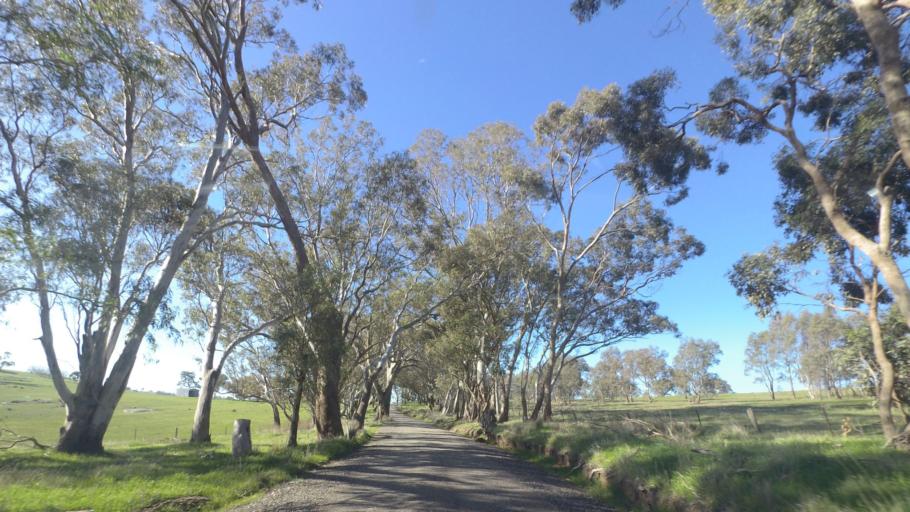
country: AU
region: Victoria
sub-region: Mount Alexander
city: Castlemaine
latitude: -36.9620
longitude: 144.3330
